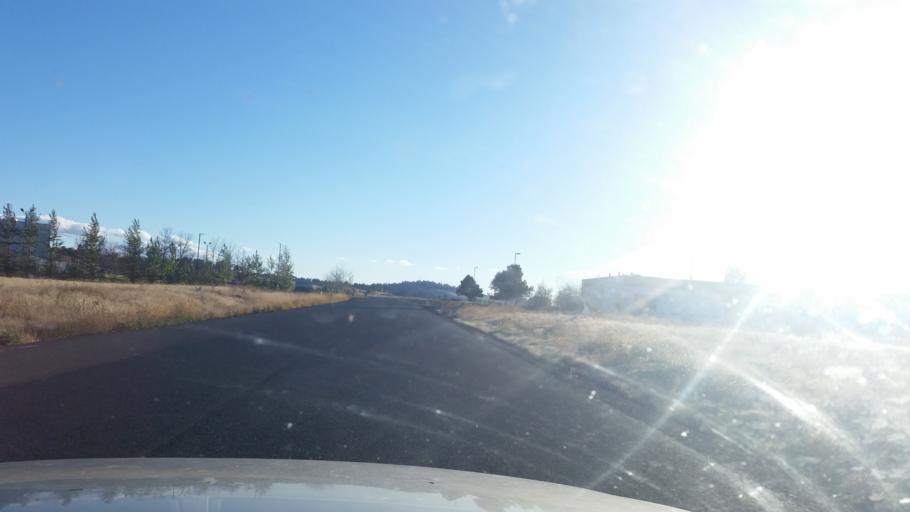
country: US
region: Washington
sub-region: Spokane County
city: Airway Heights
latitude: 47.5858
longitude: -117.5685
